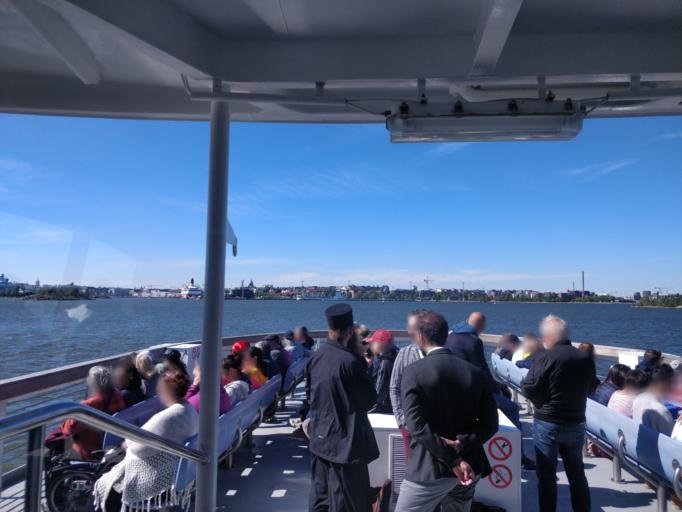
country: FI
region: Uusimaa
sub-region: Helsinki
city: Helsinki
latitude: 60.1569
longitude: 24.9826
